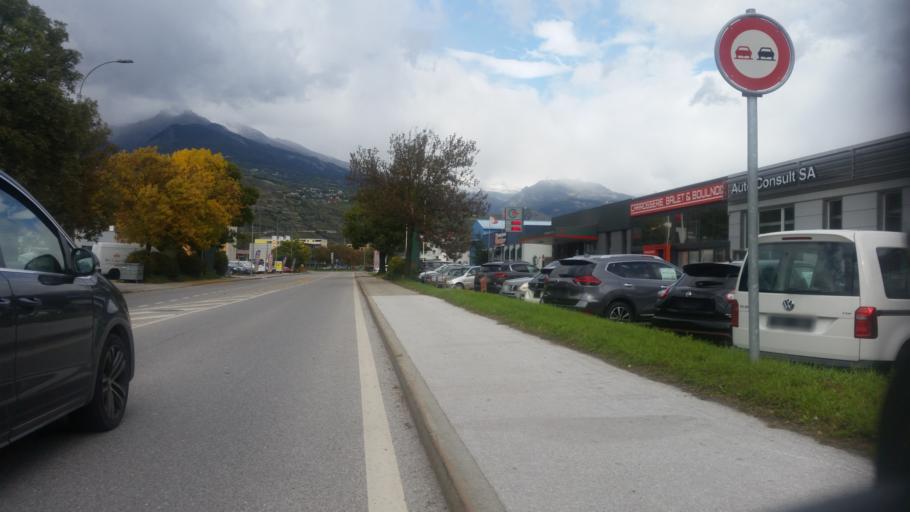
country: CH
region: Valais
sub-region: Sion District
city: Sitten
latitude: 46.2260
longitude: 7.3737
